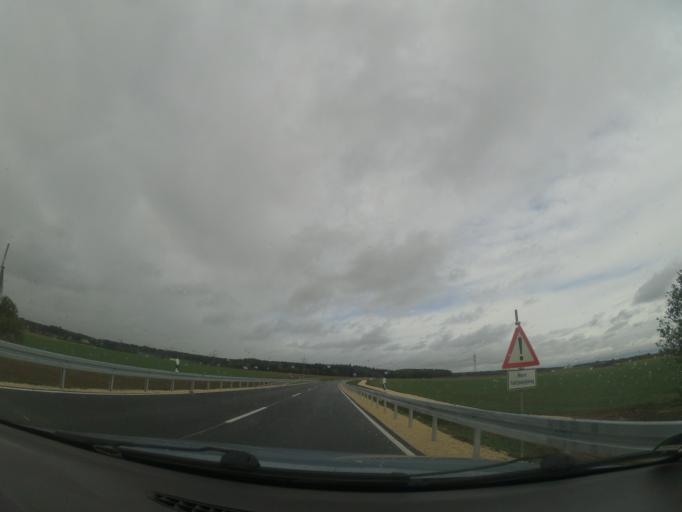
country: DE
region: Baden-Wuerttemberg
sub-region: Tuebingen Region
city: Beimerstetten
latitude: 48.4691
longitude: 9.9692
